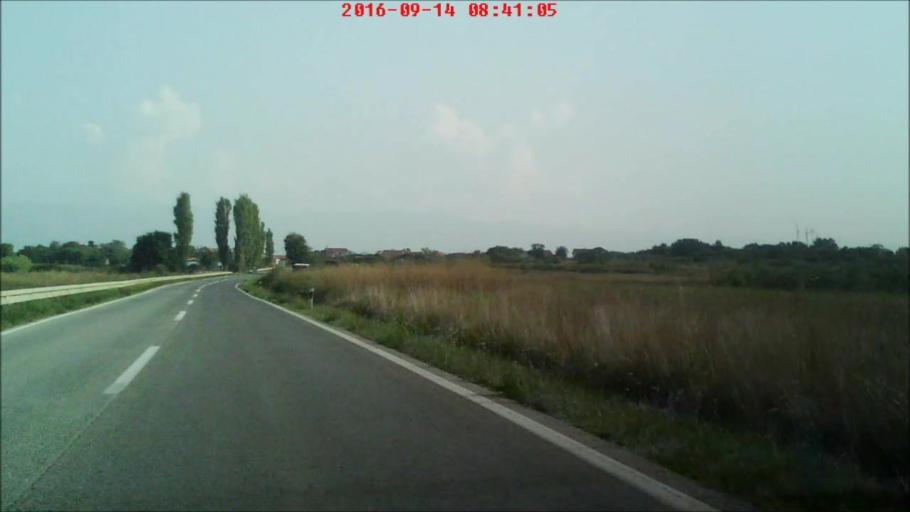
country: HR
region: Zadarska
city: Policnik
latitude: 44.1832
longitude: 15.3937
